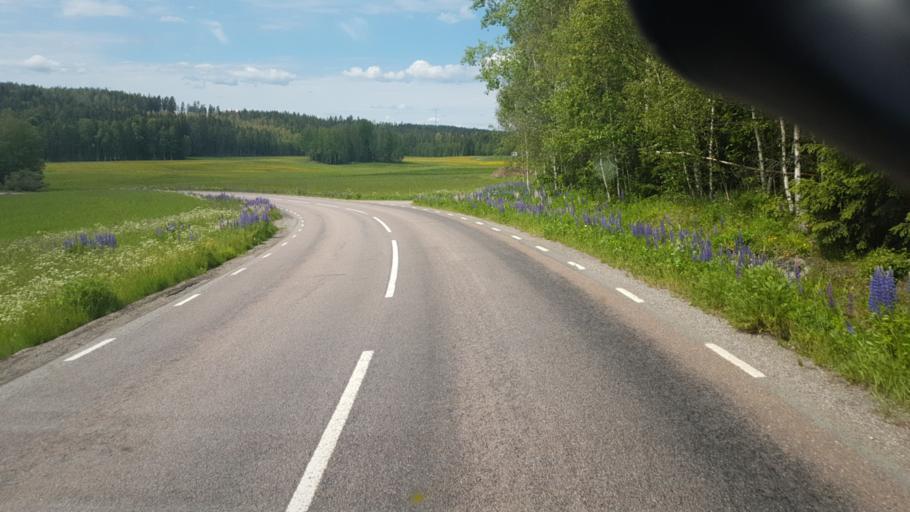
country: SE
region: Vaermland
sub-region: Eda Kommun
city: Charlottenberg
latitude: 59.8879
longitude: 12.3400
